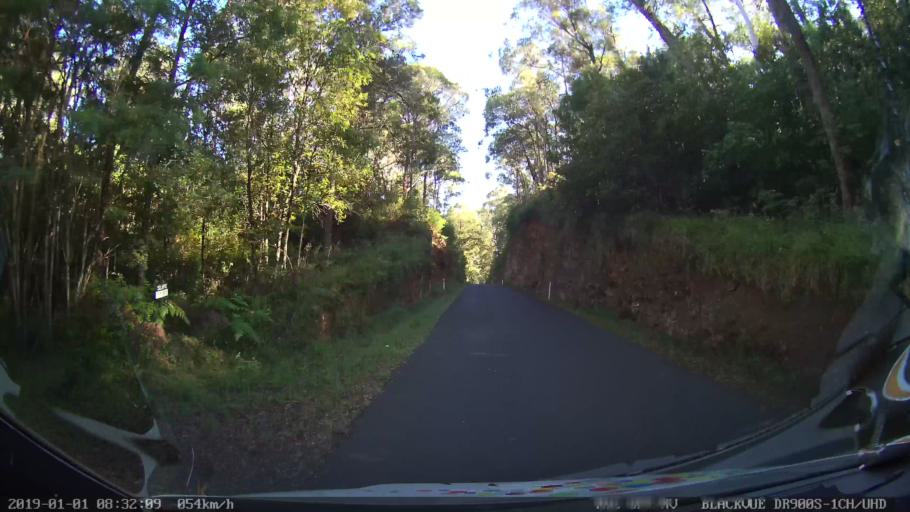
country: AU
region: New South Wales
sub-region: Snowy River
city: Jindabyne
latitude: -36.3644
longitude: 148.2058
